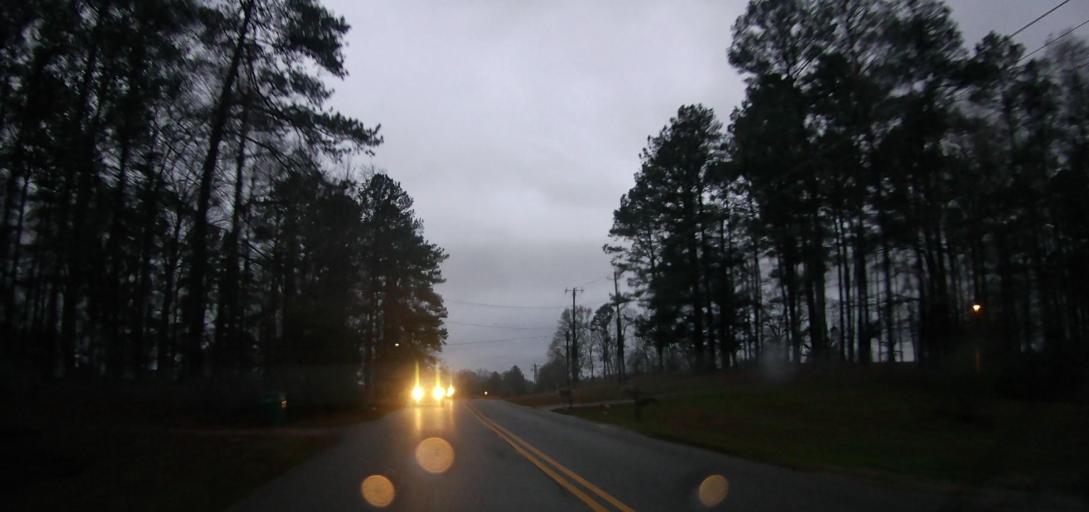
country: US
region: Alabama
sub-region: Tuscaloosa County
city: Vance
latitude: 33.1615
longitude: -87.2301
